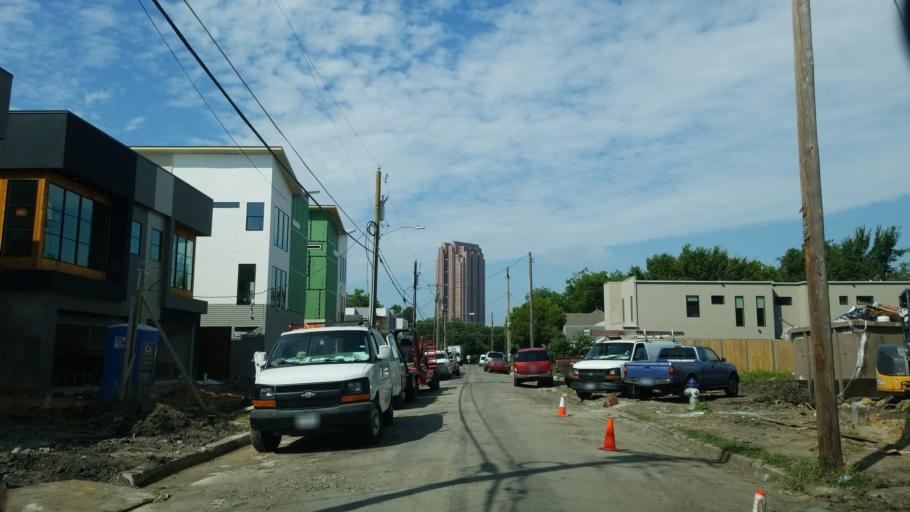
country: US
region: Texas
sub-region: Dallas County
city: Highland Park
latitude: 32.8121
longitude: -96.7845
